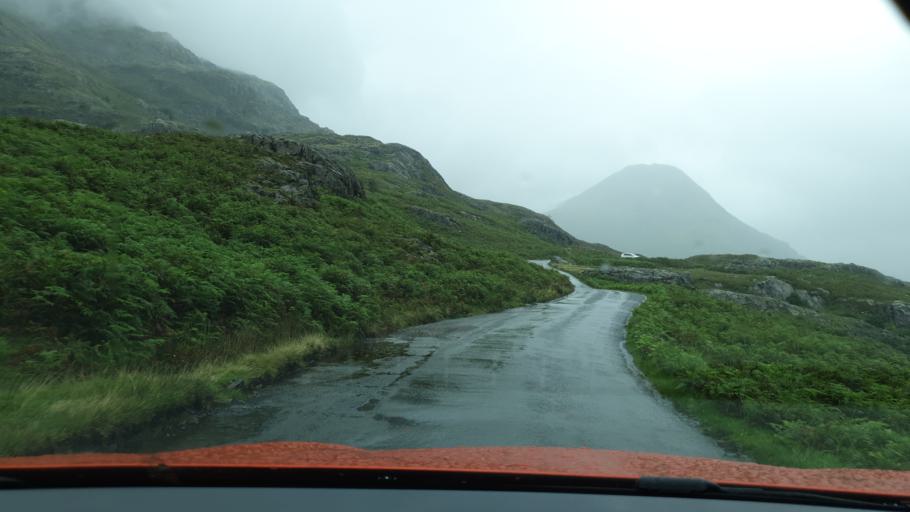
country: GB
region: England
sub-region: Cumbria
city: Seascale
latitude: 54.4406
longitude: -3.3046
